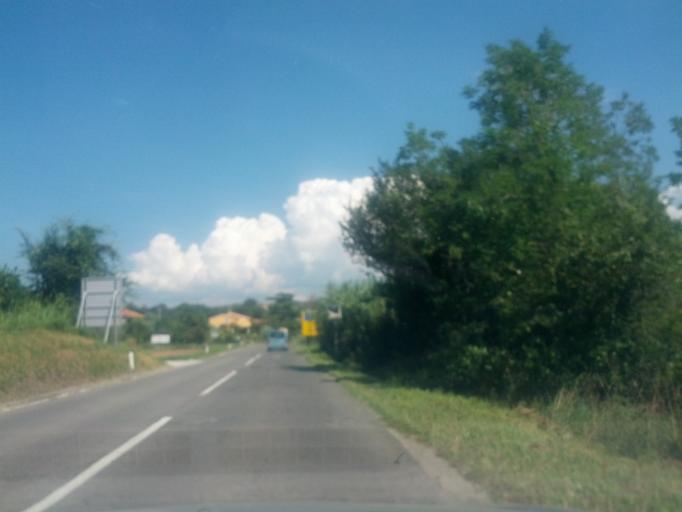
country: SI
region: Koper-Capodistria
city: Spodnje Skofije
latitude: 45.5686
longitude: 13.7725
